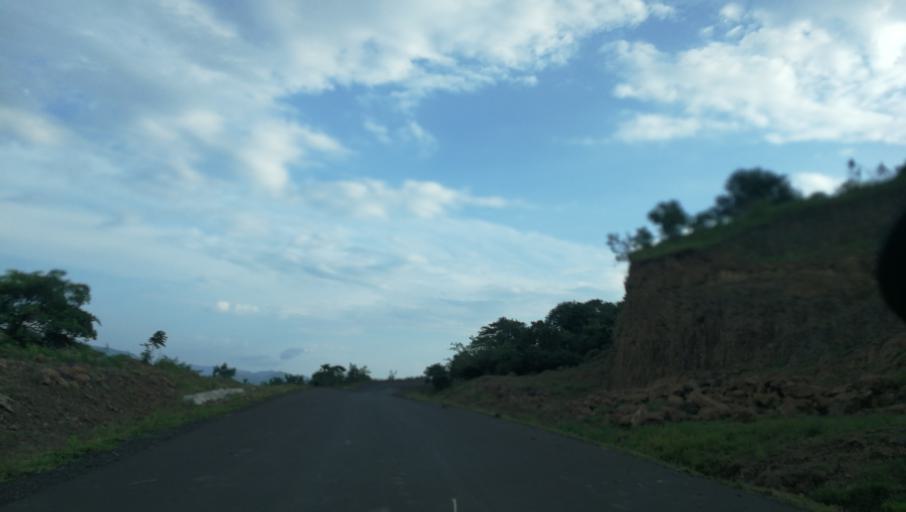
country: ET
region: Southern Nations, Nationalities, and People's Region
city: Areka
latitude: 6.8504
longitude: 37.2707
